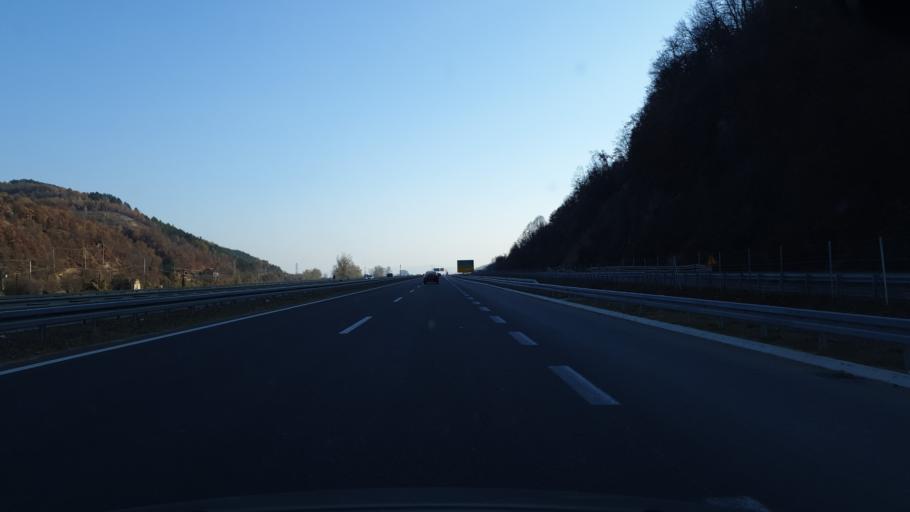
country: RS
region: Central Serbia
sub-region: Pirotski Okrug
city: Pirot
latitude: 43.2008
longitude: 22.5582
